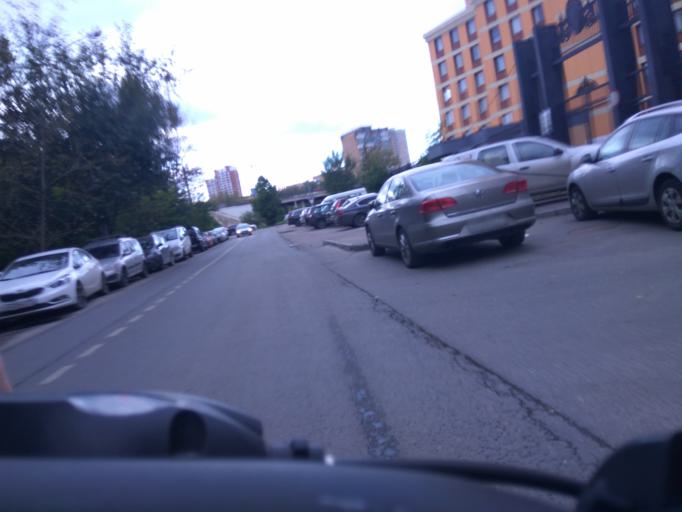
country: RU
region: Moscow
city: Slobodka
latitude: 55.8739
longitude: 37.5886
